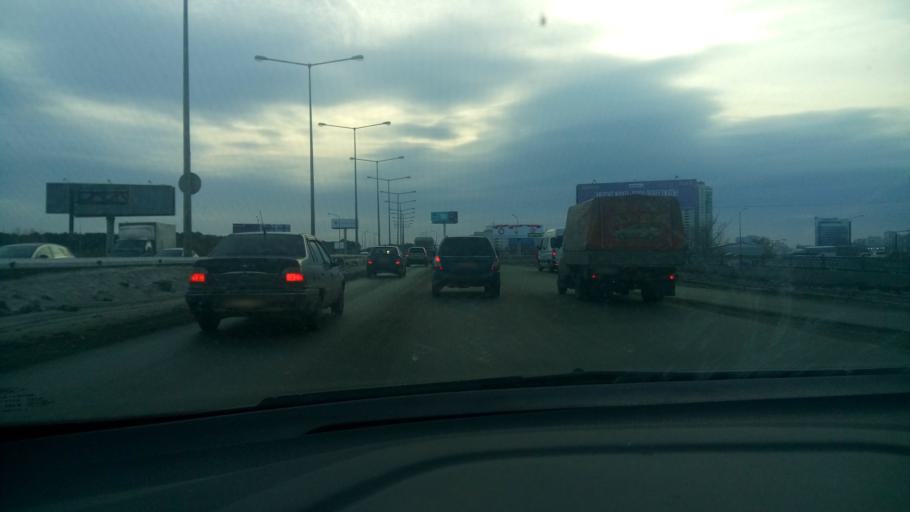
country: RU
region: Sverdlovsk
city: Yekaterinburg
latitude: 56.8004
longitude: 60.6409
